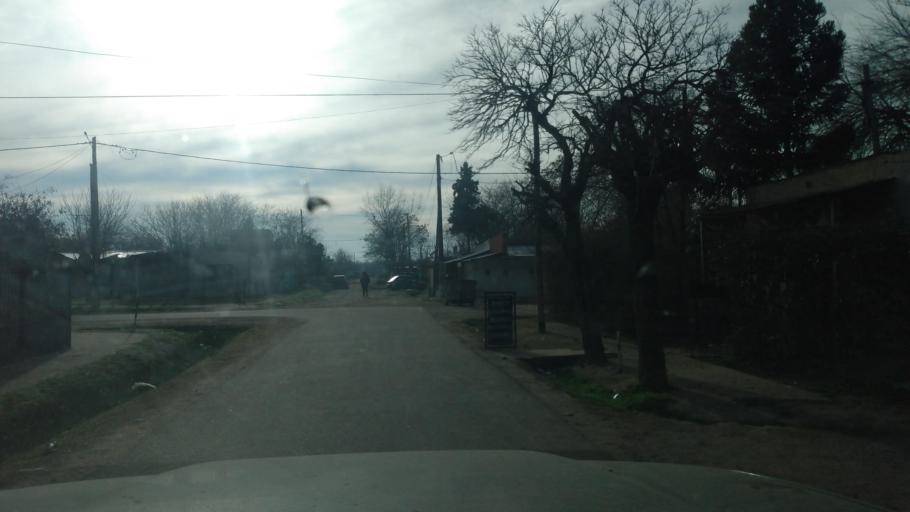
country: AR
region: Buenos Aires
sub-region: Partido de Lujan
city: Lujan
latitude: -34.5468
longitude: -59.1177
